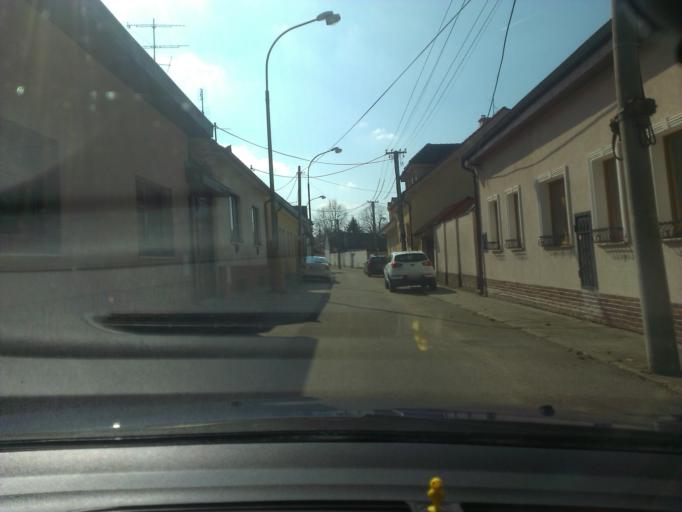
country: SK
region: Trnavsky
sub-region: Okres Trnava
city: Piestany
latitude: 48.5963
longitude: 17.8306
